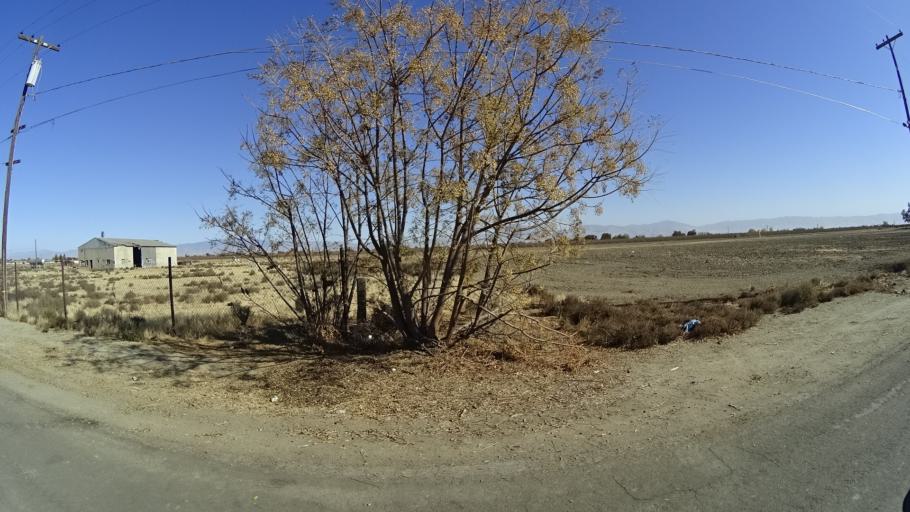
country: US
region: California
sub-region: Kern County
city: Greenfield
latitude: 35.2633
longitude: -119.0486
